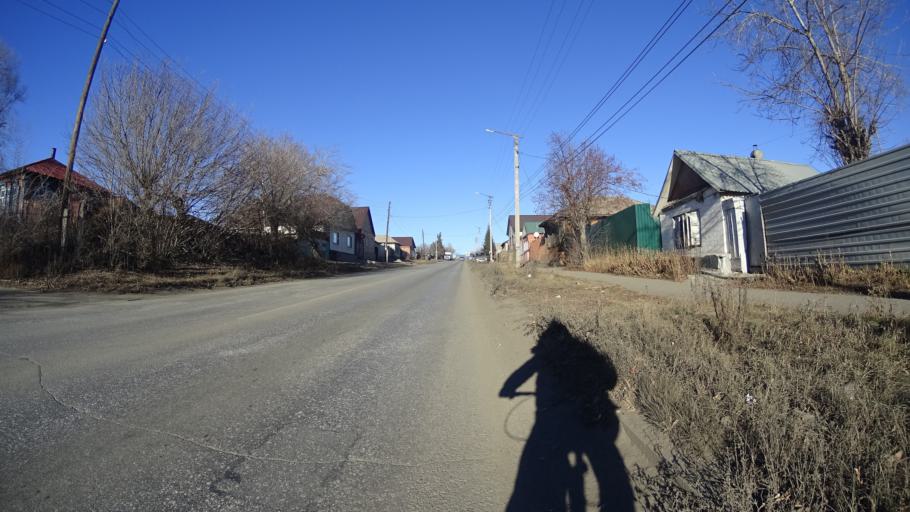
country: RU
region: Chelyabinsk
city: Troitsk
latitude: 54.1011
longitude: 61.5625
